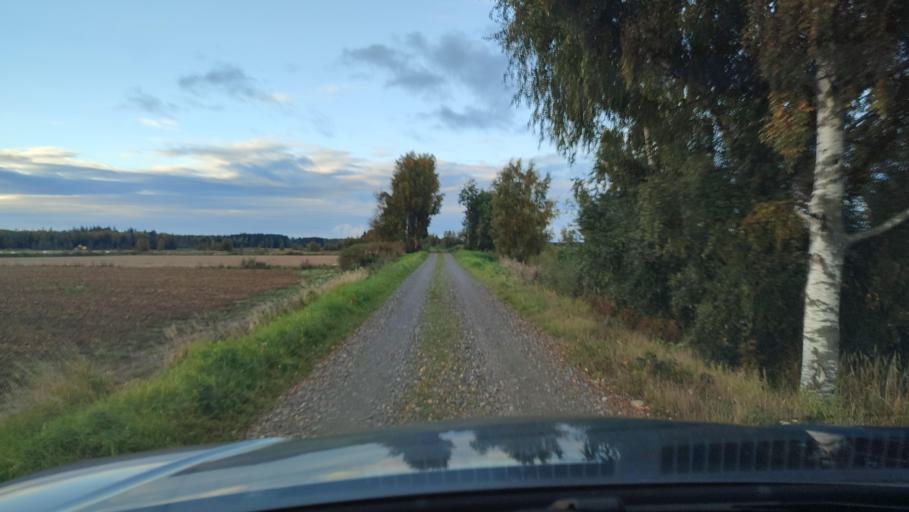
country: FI
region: Ostrobothnia
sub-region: Sydosterbotten
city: Kristinestad
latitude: 62.2367
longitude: 21.4507
